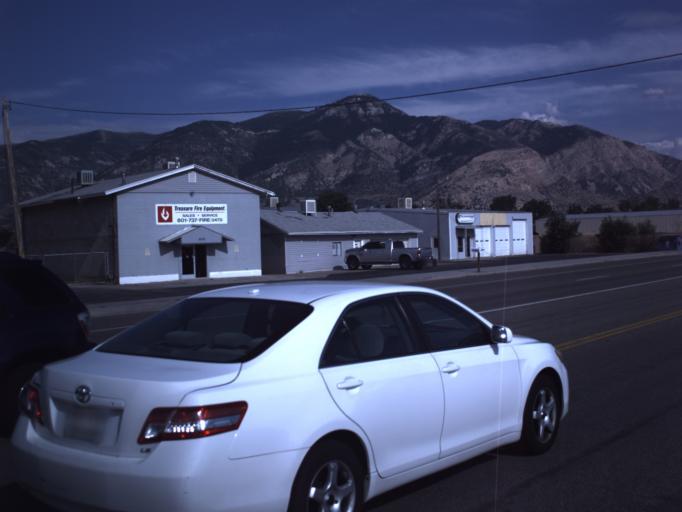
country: US
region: Utah
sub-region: Weber County
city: Pleasant View
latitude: 41.3016
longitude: -112.0010
